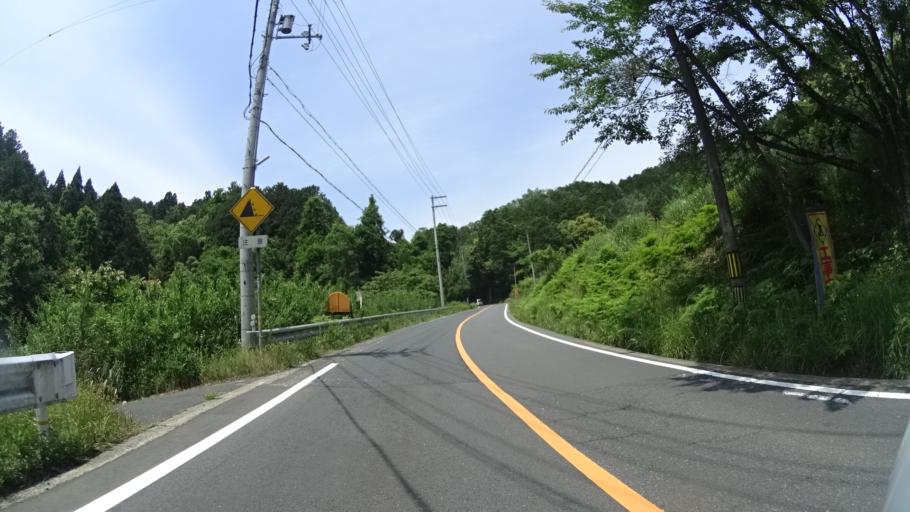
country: JP
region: Hyogo
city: Toyooka
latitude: 35.5923
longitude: 134.9174
